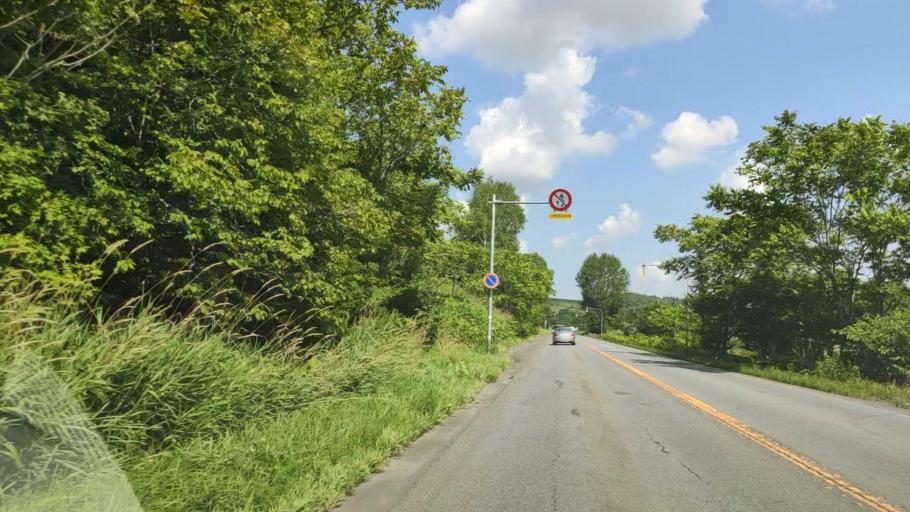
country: JP
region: Hokkaido
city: Shimo-furano
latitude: 43.5614
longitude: 142.4352
